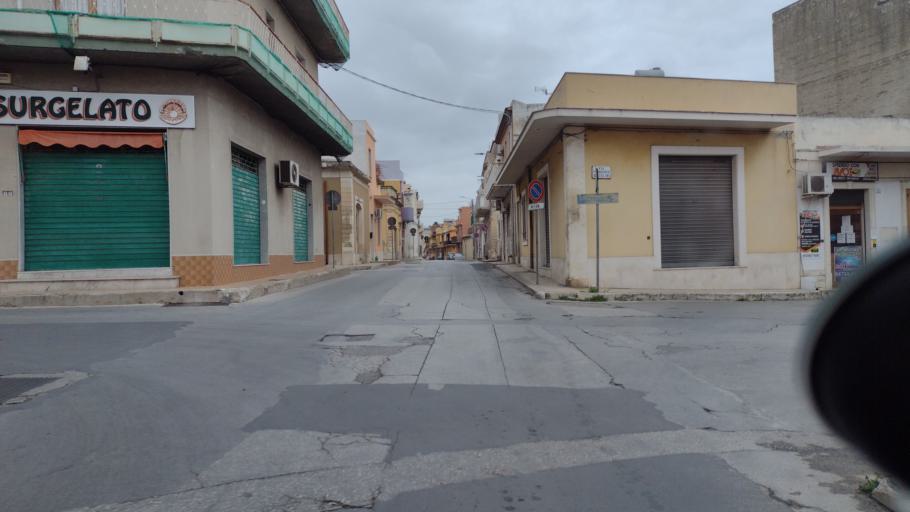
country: IT
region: Sicily
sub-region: Provincia di Siracusa
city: Avola
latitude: 36.9125
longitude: 15.1364
